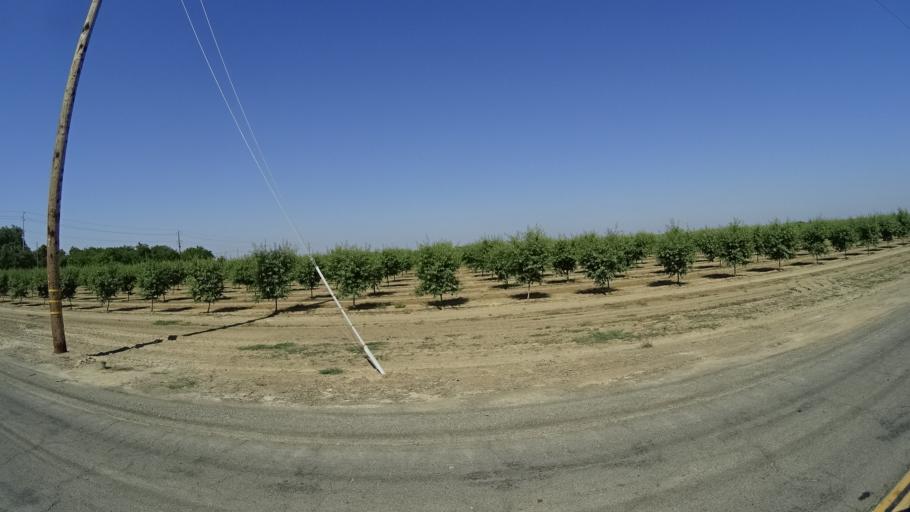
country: US
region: California
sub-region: Kings County
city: Hanford
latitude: 36.3435
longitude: -119.5830
